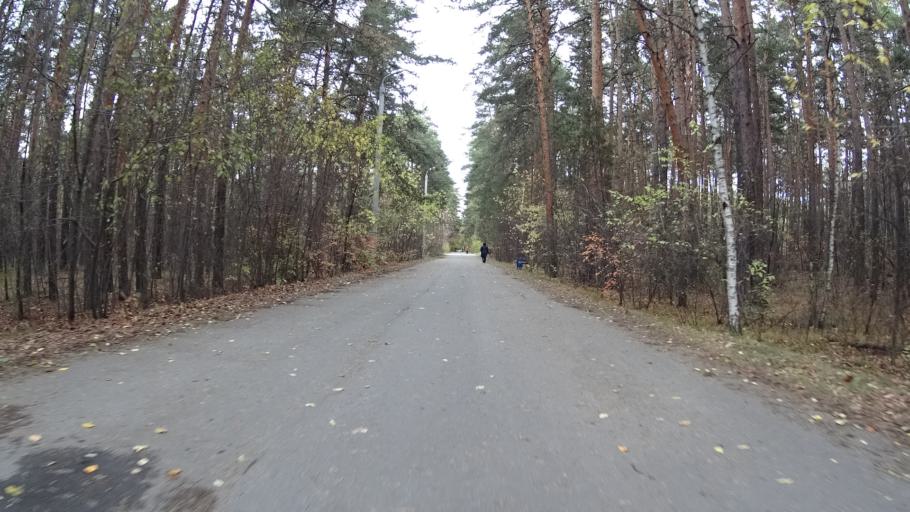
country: RU
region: Chelyabinsk
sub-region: Gorod Chelyabinsk
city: Chelyabinsk
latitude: 55.1529
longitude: 61.3586
